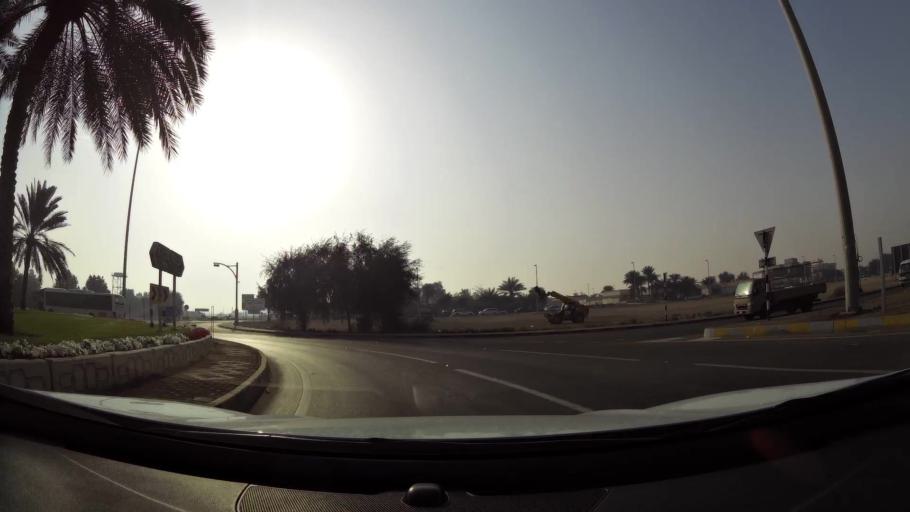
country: AE
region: Abu Dhabi
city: Abu Dhabi
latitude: 24.2782
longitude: 54.6463
